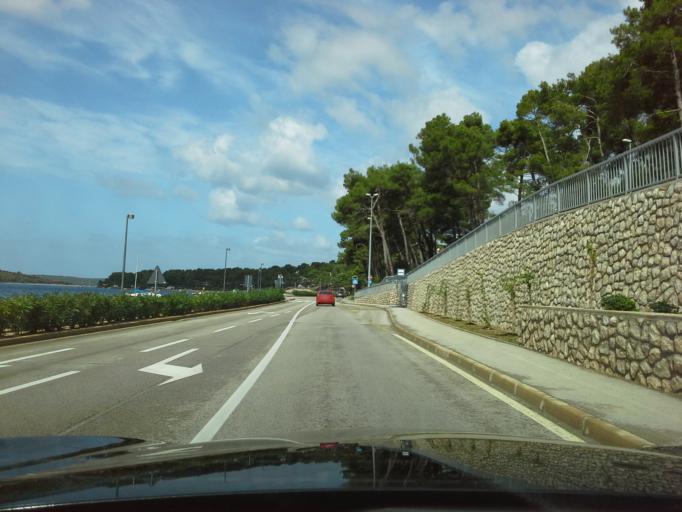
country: HR
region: Primorsko-Goranska
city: Mali Losinj
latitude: 44.5501
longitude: 14.4510
